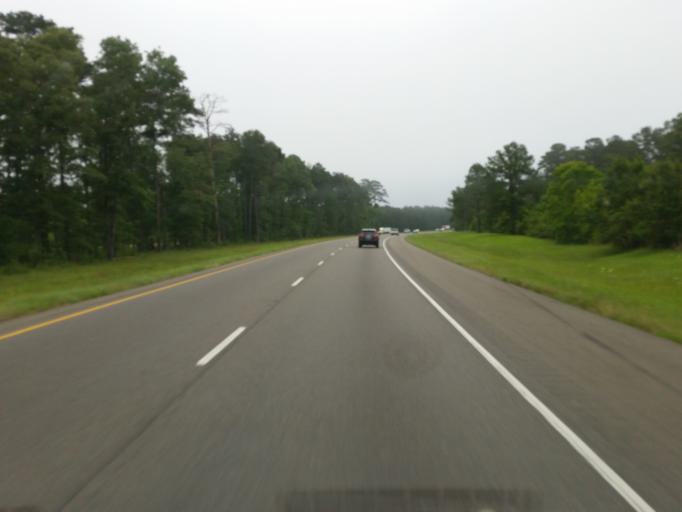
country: US
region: Louisiana
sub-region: Bossier Parish
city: Haughton
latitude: 32.5755
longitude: -93.4781
